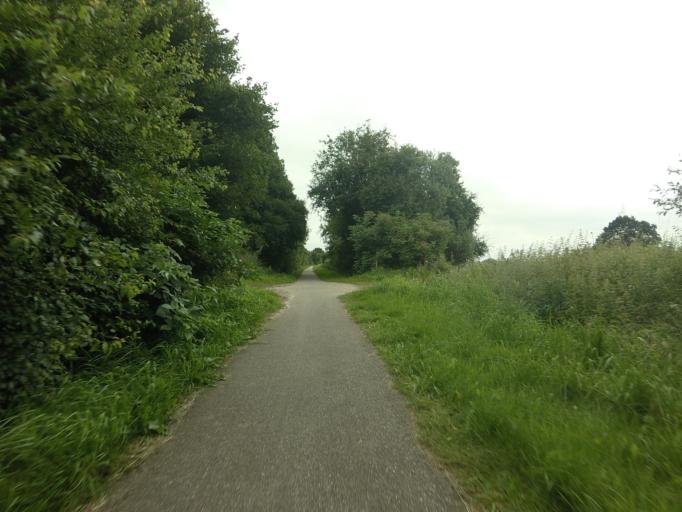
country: DK
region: Central Jutland
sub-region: Horsens Kommune
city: Braedstrup
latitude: 56.0070
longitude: 9.5869
